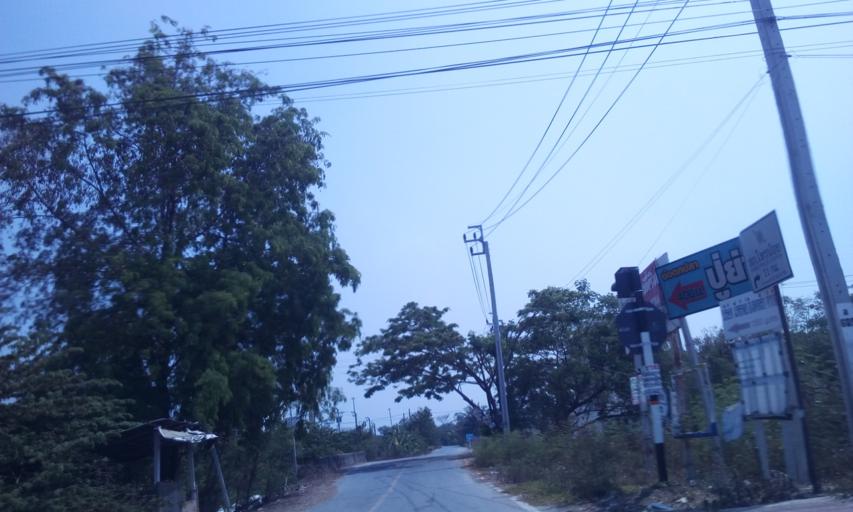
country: TH
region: Nonthaburi
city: Sai Noi
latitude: 13.9095
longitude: 100.3267
